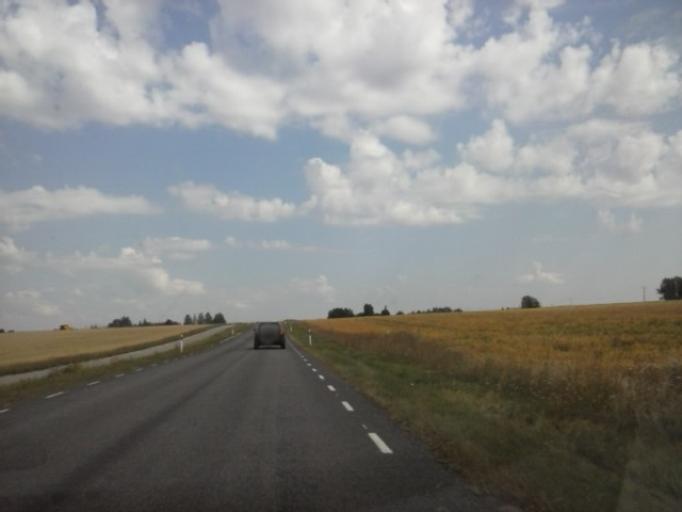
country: EE
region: Jogevamaa
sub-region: Tabivere vald
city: Tabivere
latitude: 58.5101
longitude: 26.6825
